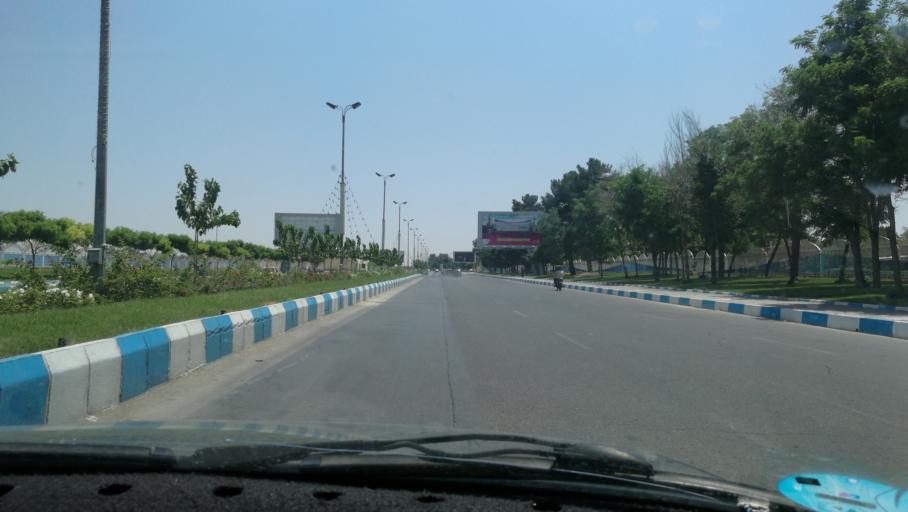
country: IR
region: Razavi Khorasan
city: Mashhad
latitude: 36.2371
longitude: 59.6296
